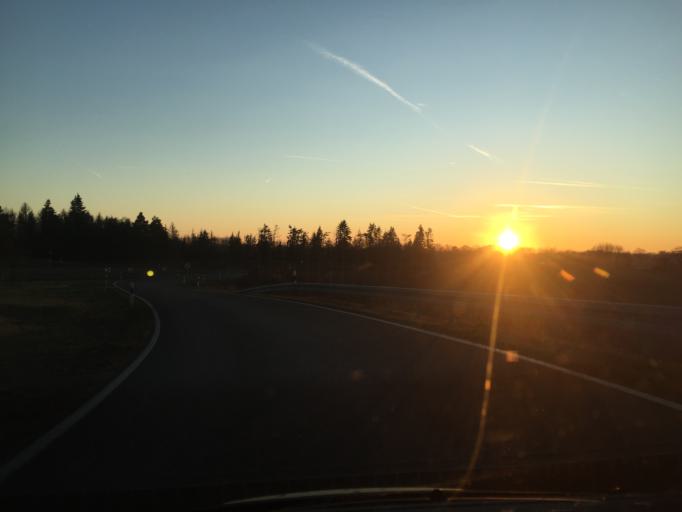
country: DE
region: Lower Saxony
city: Burgdorf
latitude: 52.4619
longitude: 9.9881
